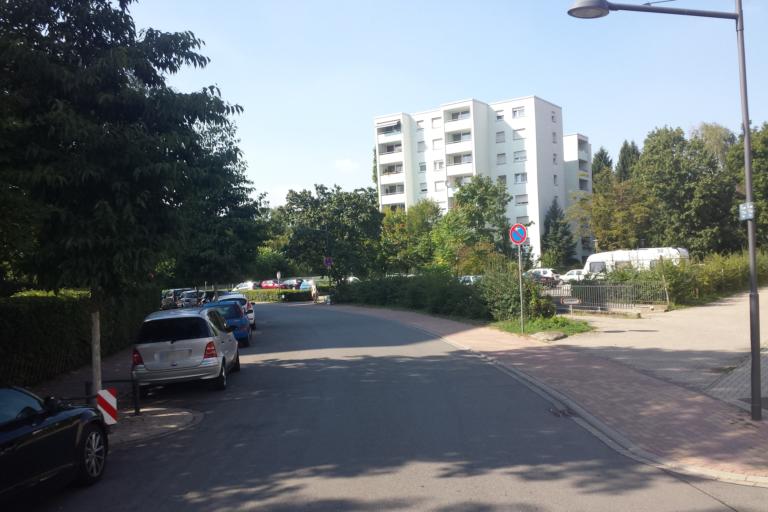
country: DE
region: Baden-Wuerttemberg
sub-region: Karlsruhe Region
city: Eppelheim
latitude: 49.4072
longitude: 8.6314
